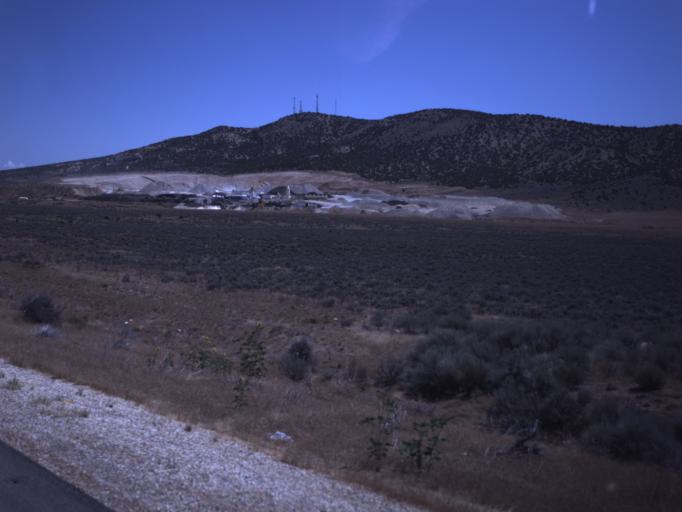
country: US
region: Utah
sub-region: Uintah County
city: Maeser
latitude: 40.4418
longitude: -109.6406
